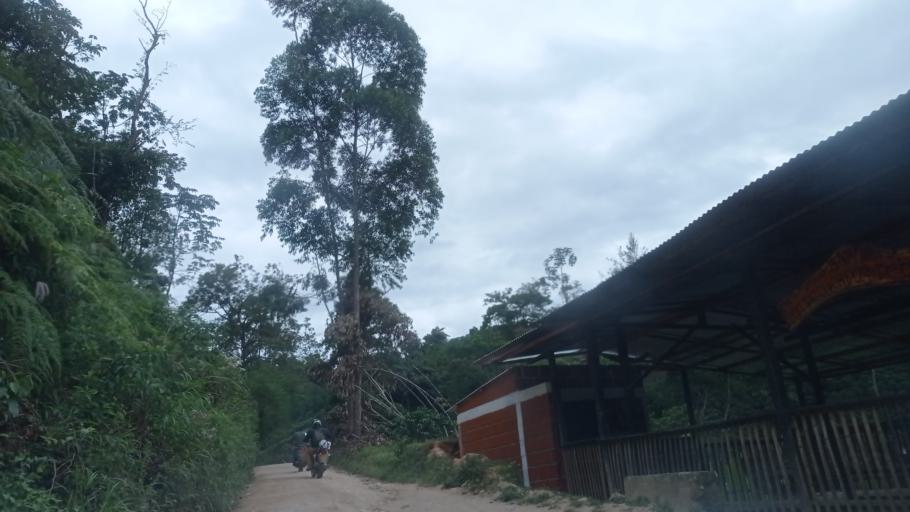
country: CO
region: Huila
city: Garzon
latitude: 2.1050
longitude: -75.6296
